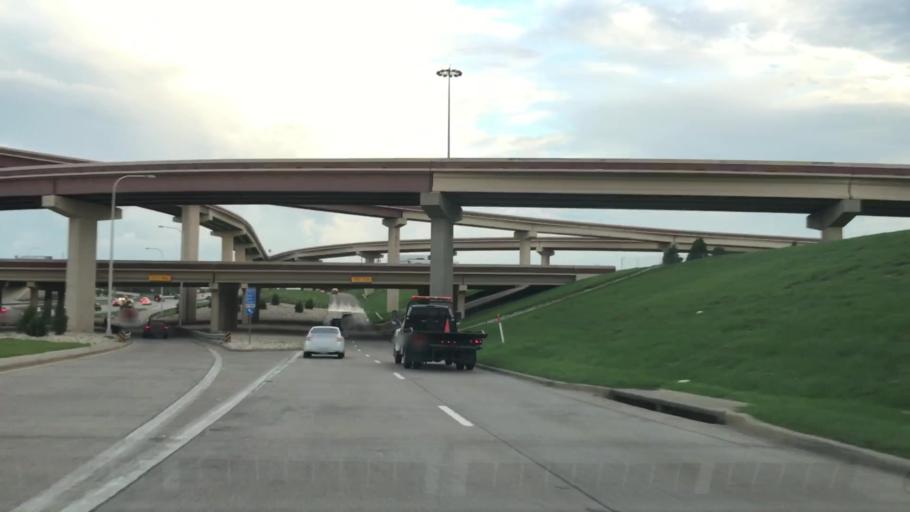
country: US
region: Texas
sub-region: Dallas County
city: Addison
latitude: 33.0138
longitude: -96.8299
